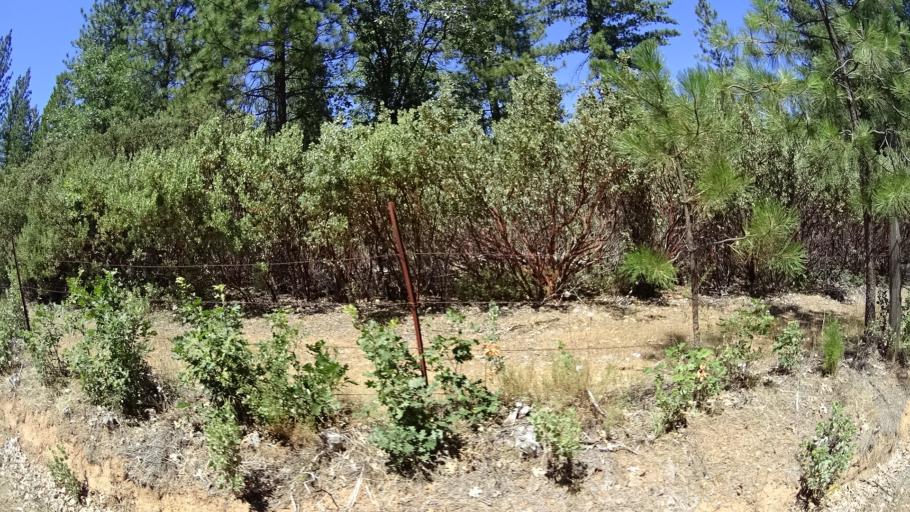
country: US
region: California
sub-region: Calaveras County
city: Mountain Ranch
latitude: 38.3190
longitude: -120.5385
